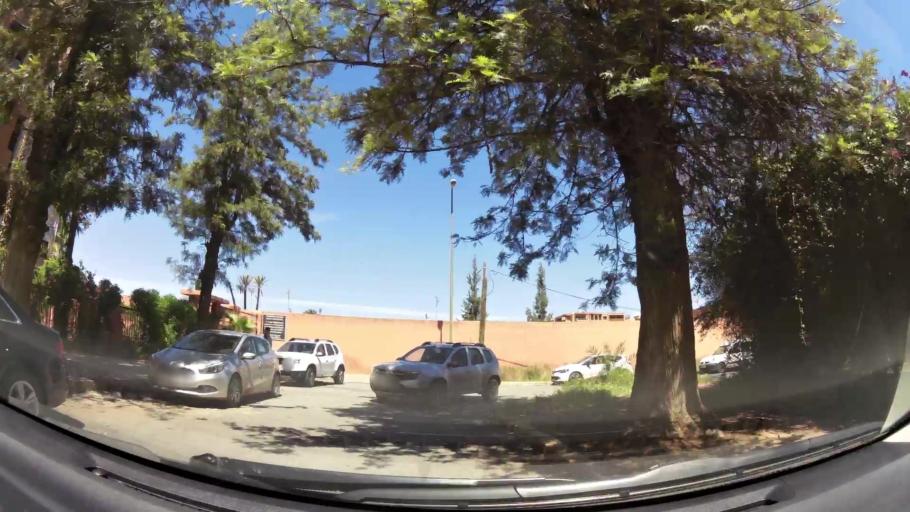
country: MA
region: Marrakech-Tensift-Al Haouz
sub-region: Marrakech
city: Marrakesh
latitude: 31.6260
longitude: -8.0064
